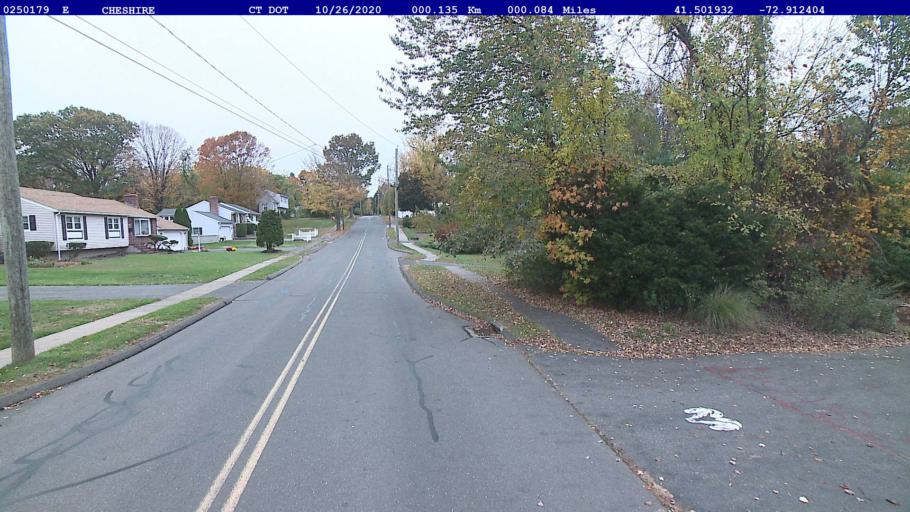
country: US
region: Connecticut
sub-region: New Haven County
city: Cheshire
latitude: 41.5019
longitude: -72.9124
